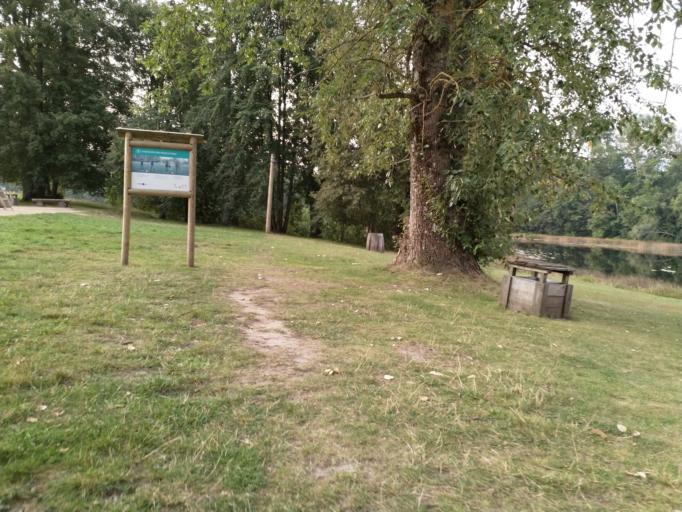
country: LV
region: Kuldigas Rajons
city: Kuldiga
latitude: 56.9682
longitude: 21.9812
